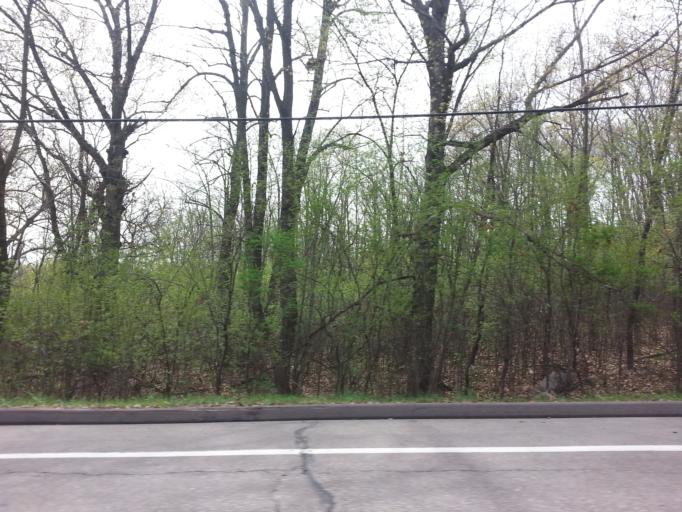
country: US
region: Minnesota
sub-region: Scott County
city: Savage
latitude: 44.8255
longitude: -93.3778
